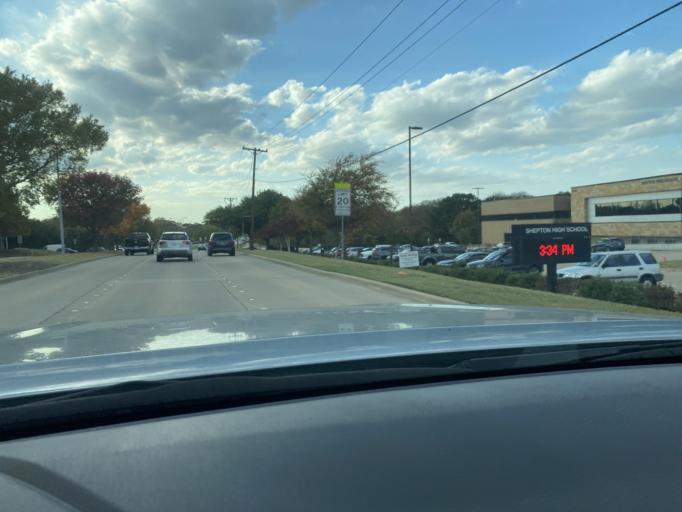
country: US
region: Texas
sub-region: Dallas County
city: Addison
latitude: 33.0162
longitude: -96.8111
